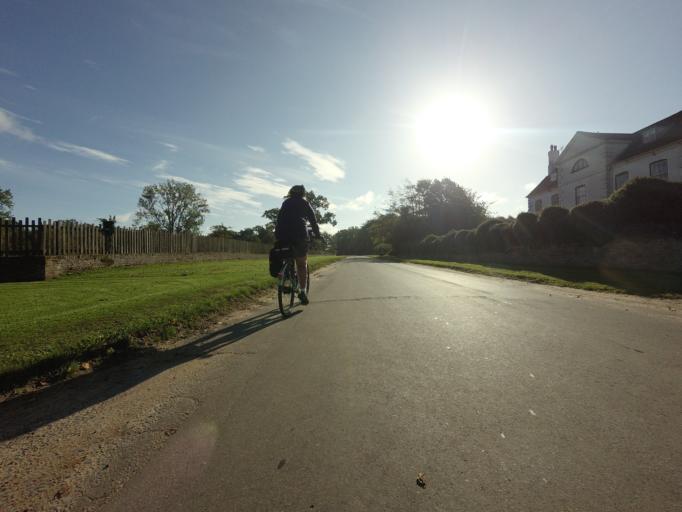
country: GB
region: England
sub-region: Norfolk
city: Dersingham
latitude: 52.8189
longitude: 0.6508
